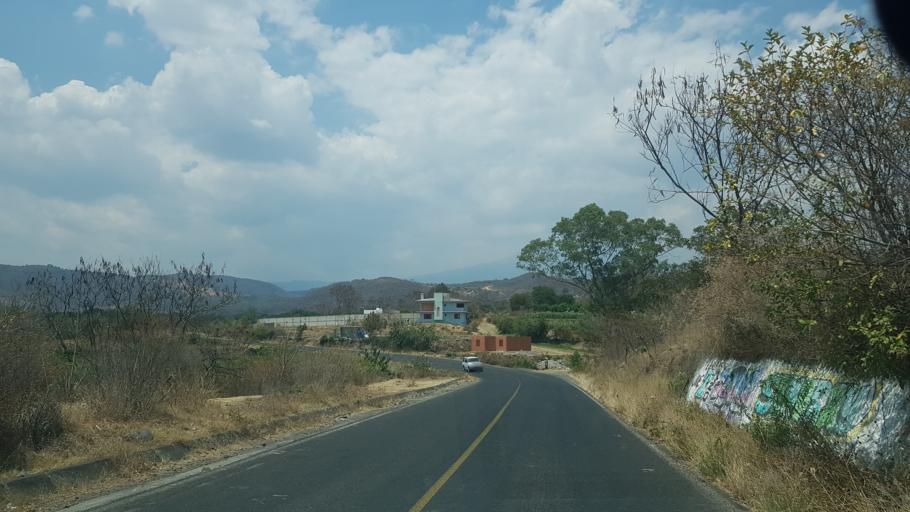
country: MX
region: Puebla
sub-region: Atzitzihuacan
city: Santiago Atzitzihuacan
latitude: 18.8375
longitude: -98.5769
